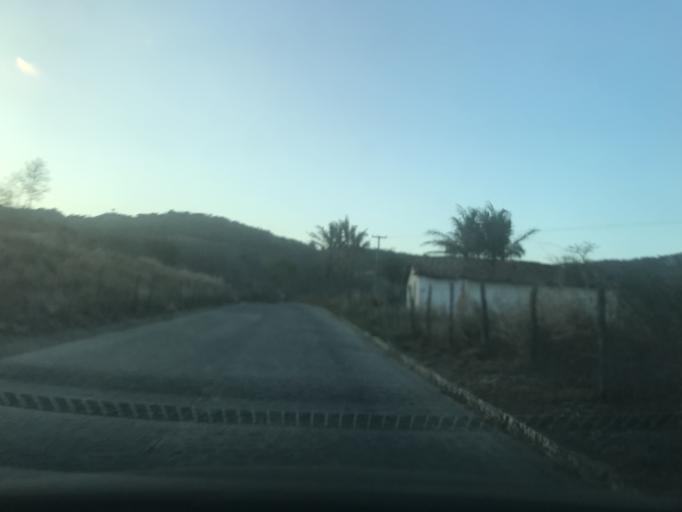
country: BR
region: Pernambuco
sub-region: Bezerros
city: Bezerros
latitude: -8.1924
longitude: -35.7574
